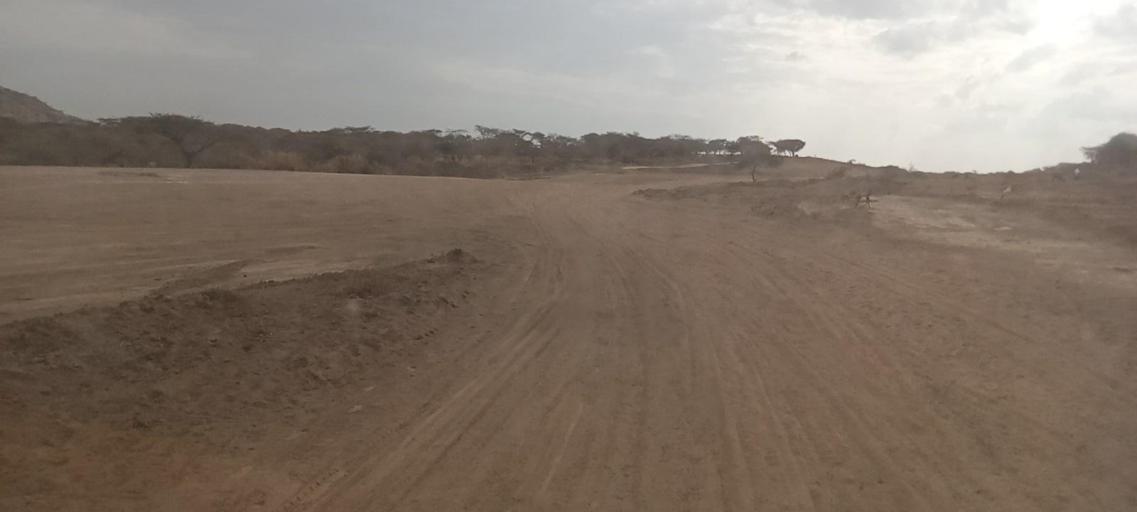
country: ET
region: Oromiya
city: Ziway
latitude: 7.7963
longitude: 38.6299
